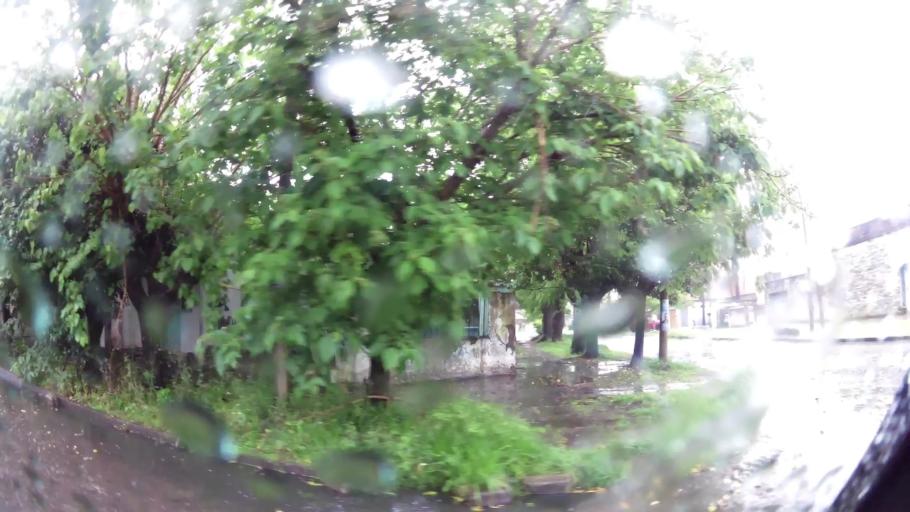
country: AR
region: Buenos Aires
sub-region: Partido de Lanus
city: Lanus
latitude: -34.7097
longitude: -58.4181
